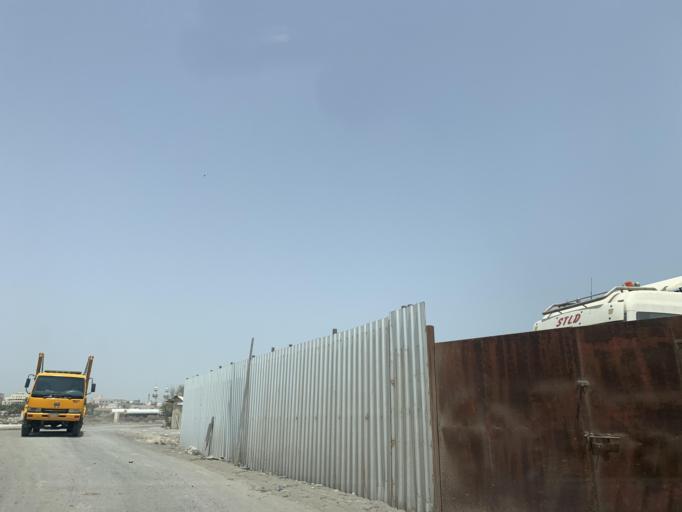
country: BH
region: Northern
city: Sitrah
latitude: 26.1360
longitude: 50.5950
